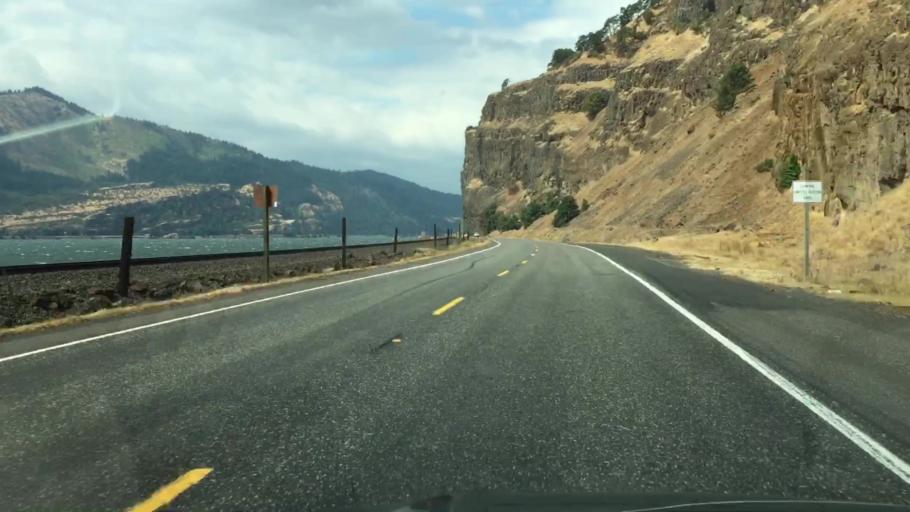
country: US
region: Washington
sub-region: Klickitat County
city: White Salmon
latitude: 45.6992
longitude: -121.4127
